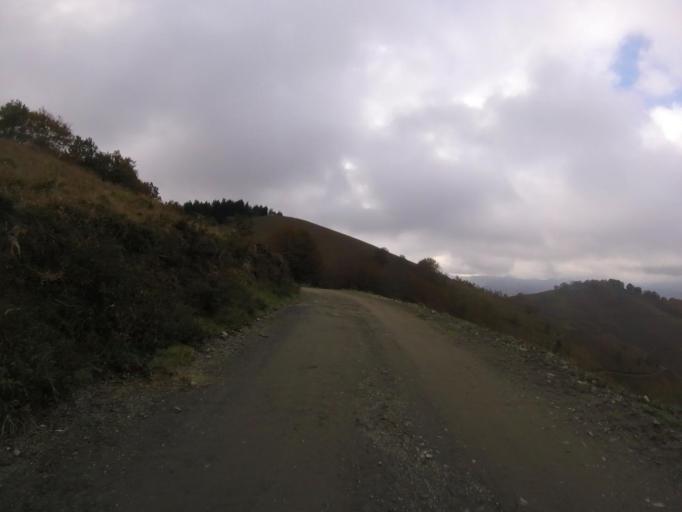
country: ES
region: Navarre
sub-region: Provincia de Navarra
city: Goizueta
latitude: 43.2053
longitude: -1.8244
